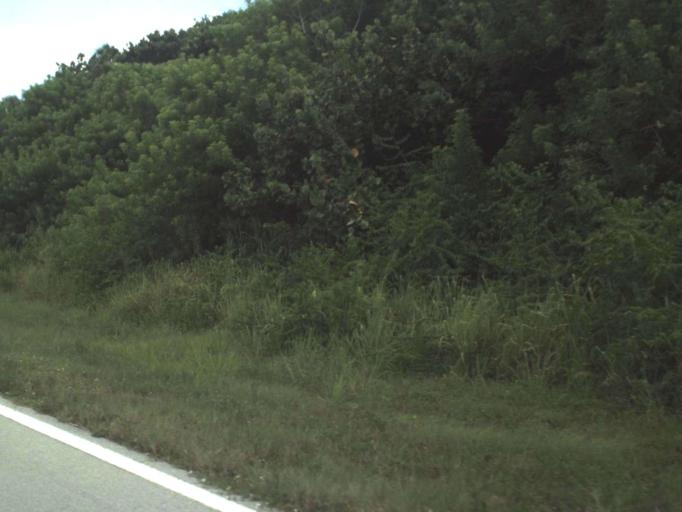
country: US
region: Florida
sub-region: Saint Lucie County
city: Hutchinson Island South
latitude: 27.3080
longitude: -80.2217
